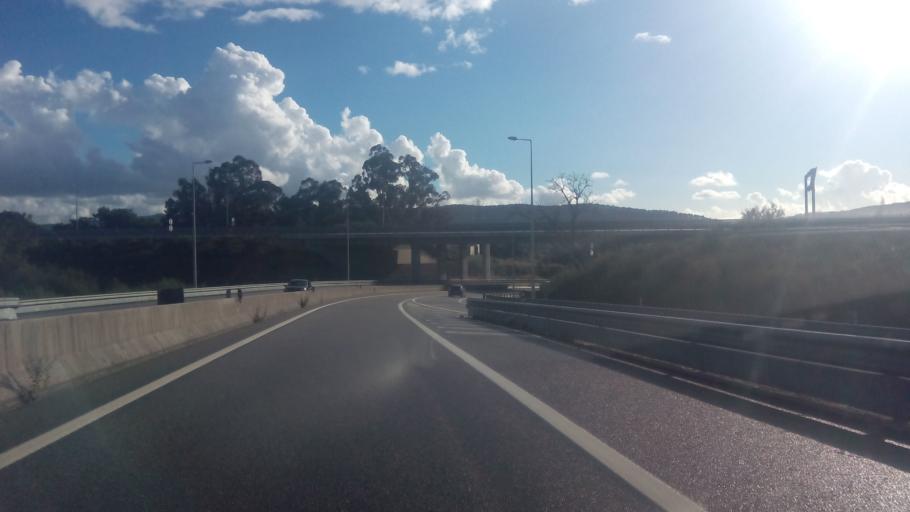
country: PT
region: Porto
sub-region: Valongo
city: Campo
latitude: 41.1829
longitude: -8.4514
